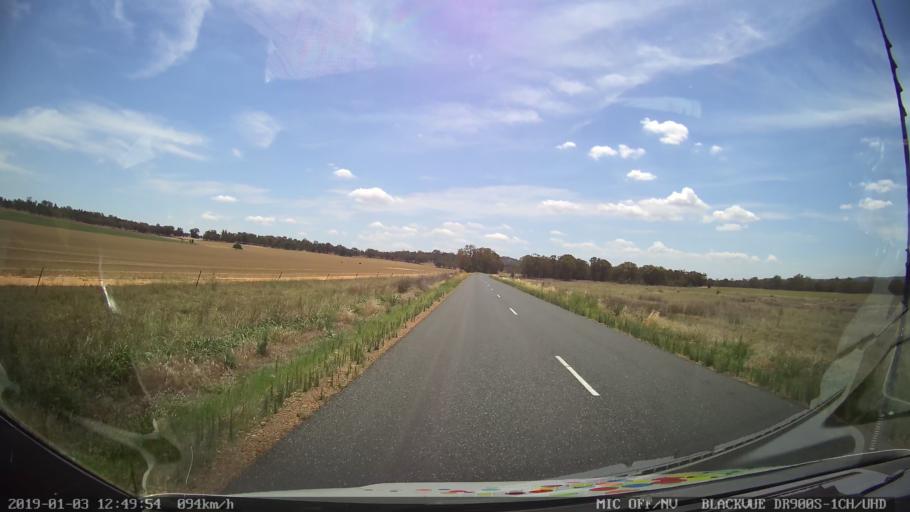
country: AU
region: New South Wales
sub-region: Weddin
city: Grenfell
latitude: -33.6976
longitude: 148.2648
